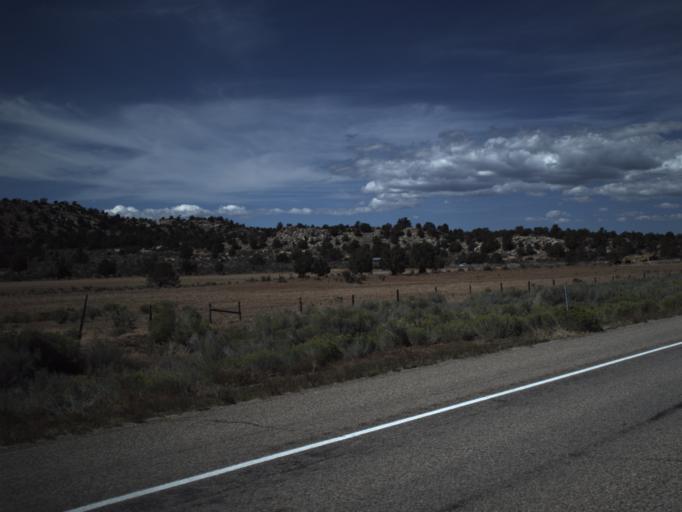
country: US
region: Utah
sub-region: Washington County
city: Ivins
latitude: 37.2600
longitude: -113.6343
